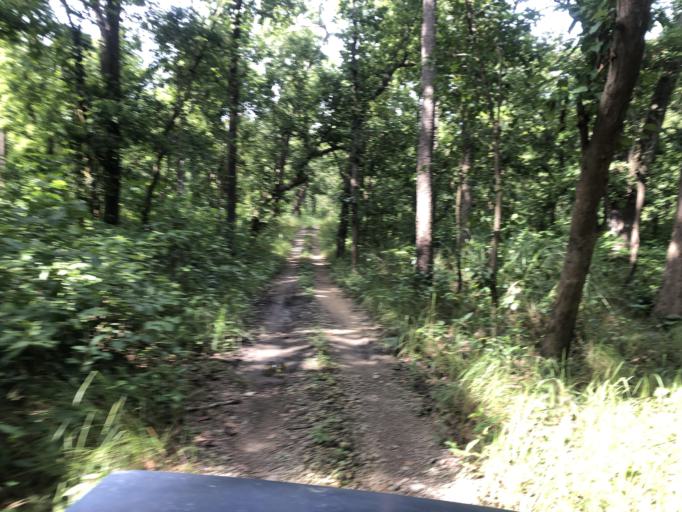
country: NP
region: Far Western
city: Tikapur
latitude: 28.5448
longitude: 81.2864
